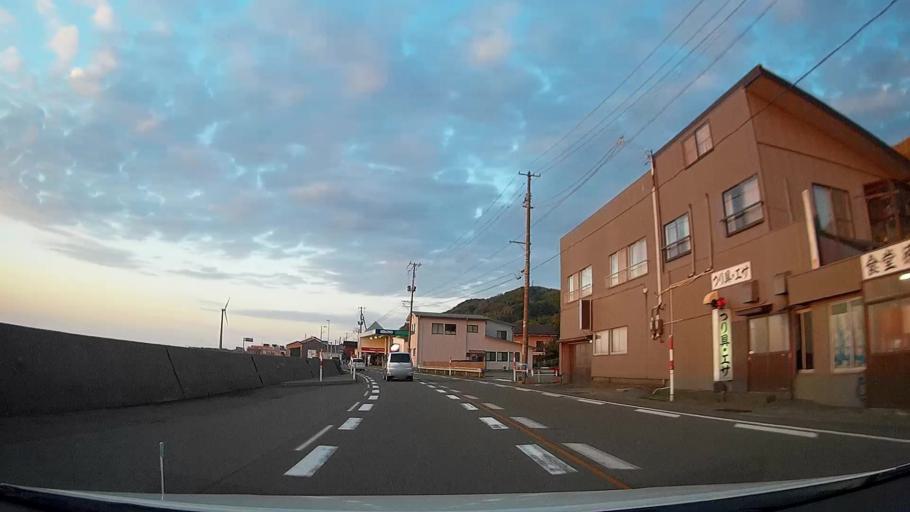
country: JP
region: Niigata
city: Joetsu
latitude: 37.1571
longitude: 138.0828
